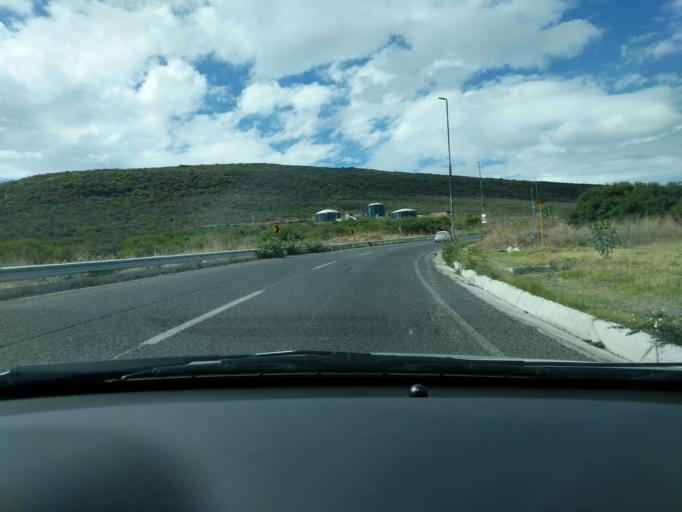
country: MX
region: Queretaro
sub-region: El Marques
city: La Pradera
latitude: 20.6607
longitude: -100.3434
